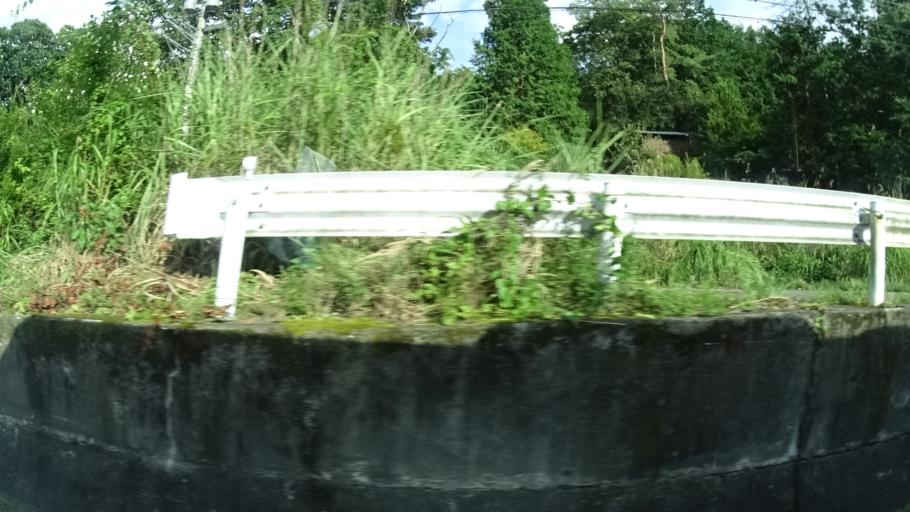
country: JP
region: Tochigi
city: Nikko
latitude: 36.6597
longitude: 139.4592
